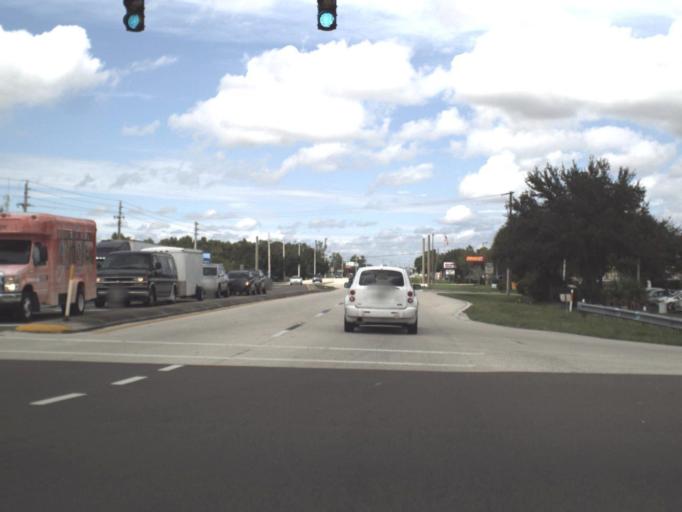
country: US
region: Florida
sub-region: Lee County
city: Villas
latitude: 26.5465
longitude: -81.8524
